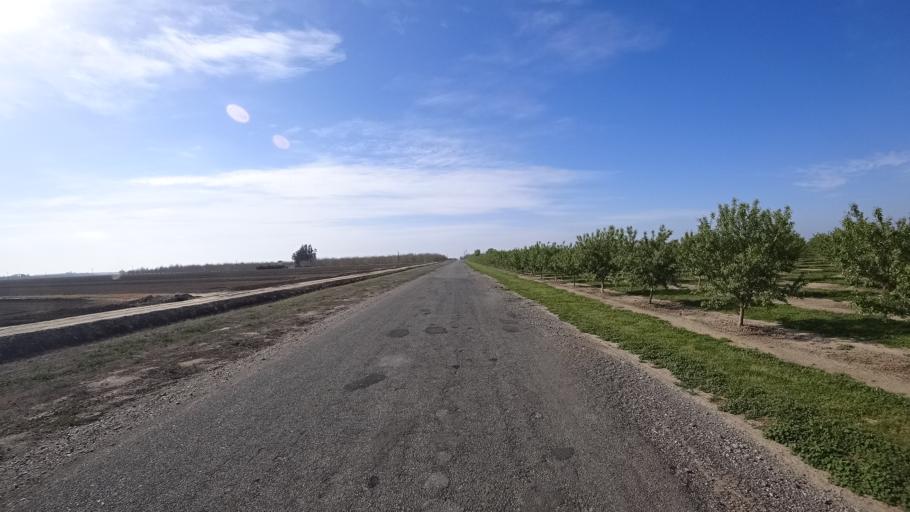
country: US
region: California
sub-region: Glenn County
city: Hamilton City
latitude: 39.6264
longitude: -122.0463
